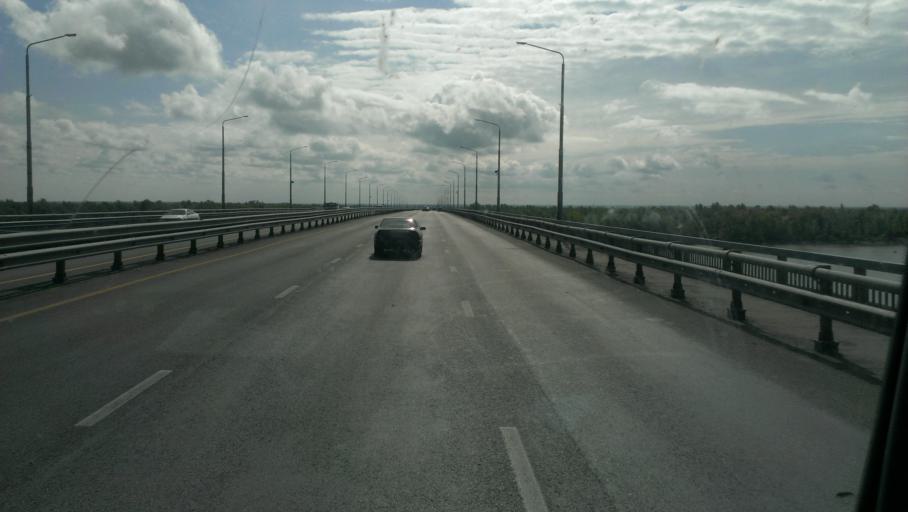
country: RU
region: Altai Krai
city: Zaton
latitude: 53.3243
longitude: 83.8007
